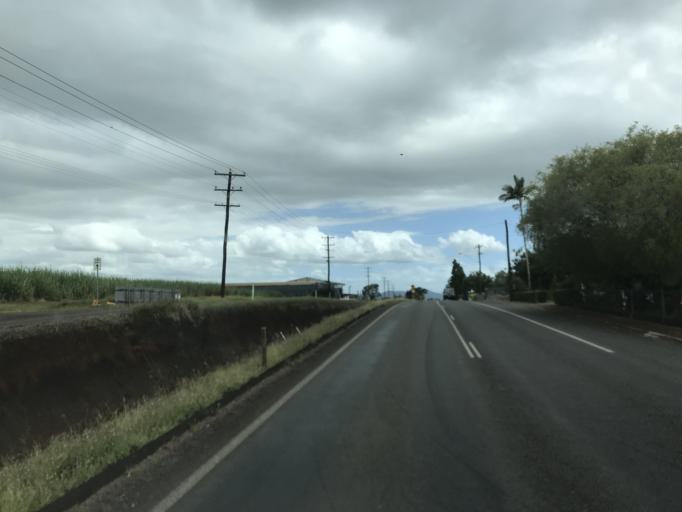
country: AU
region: Queensland
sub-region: Cassowary Coast
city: Innisfail
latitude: -17.5962
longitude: 145.9962
